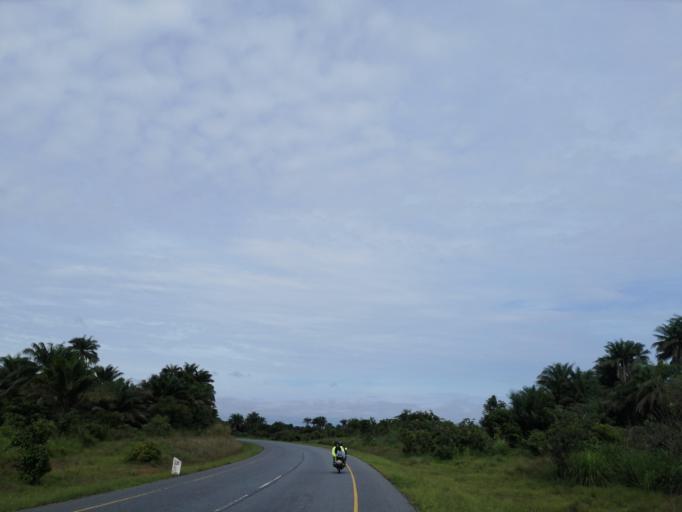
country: SL
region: Northern Province
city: Port Loko
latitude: 8.7700
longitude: -12.8822
